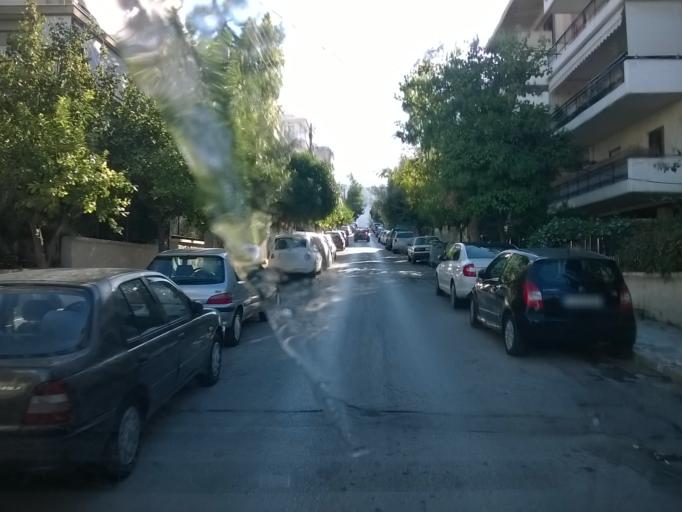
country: GR
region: Attica
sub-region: Nomarchia Athinas
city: Dhafni
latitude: 37.9439
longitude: 23.7364
